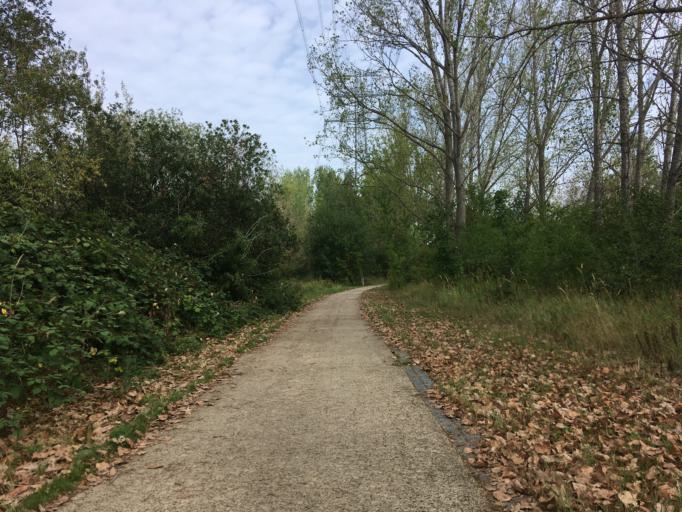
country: DE
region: Berlin
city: Falkenberg
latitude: 52.5569
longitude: 13.5429
